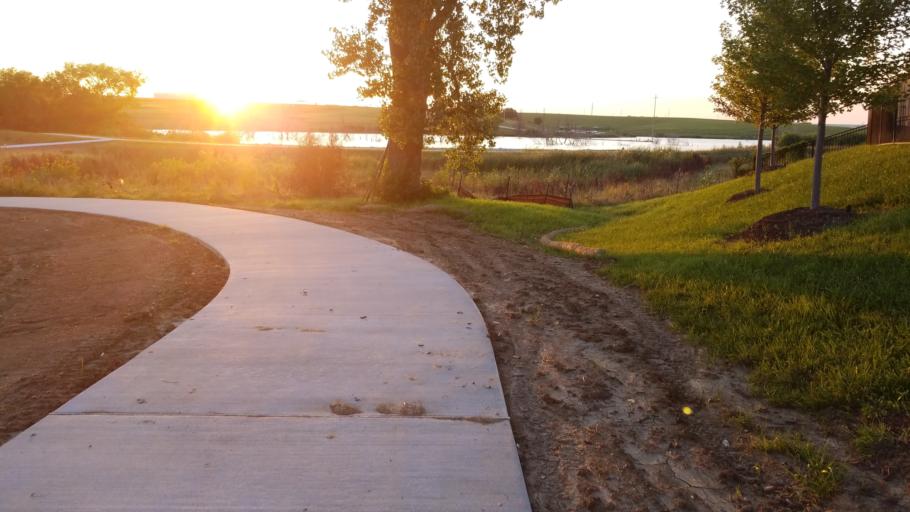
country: US
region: Nebraska
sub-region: Sarpy County
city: Chalco
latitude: 41.1596
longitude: -96.1098
